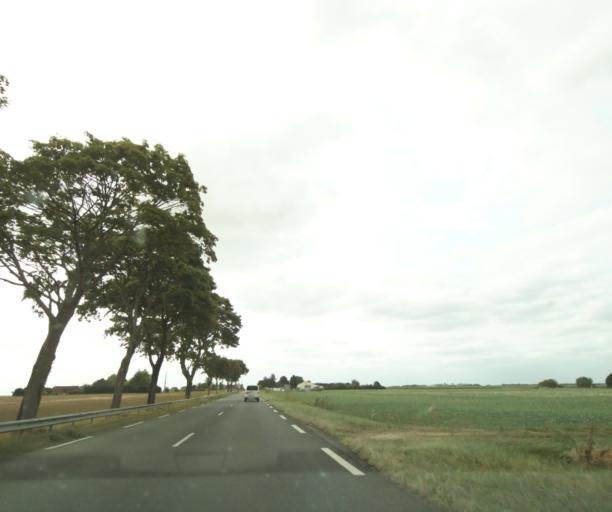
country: FR
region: Centre
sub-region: Departement d'Indre-et-Loire
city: Reignac-sur-Indre
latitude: 47.1944
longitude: 0.9236
